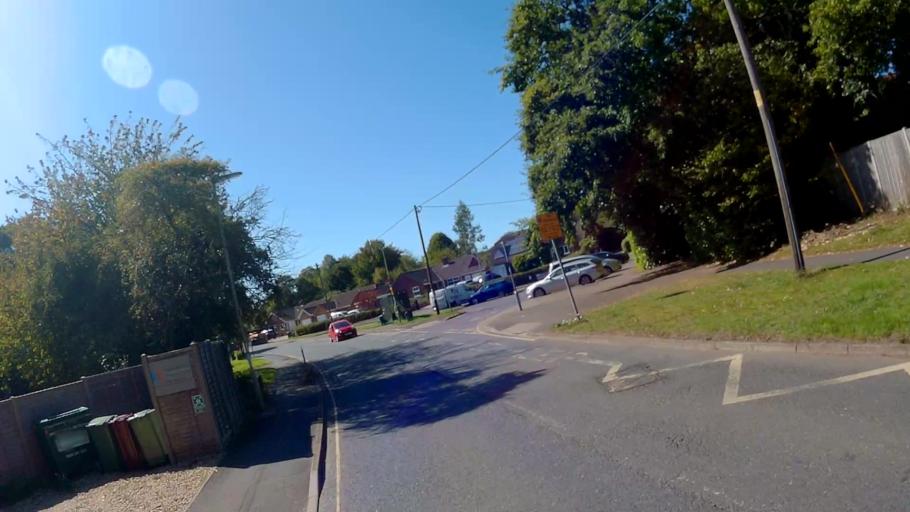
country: GB
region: England
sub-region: Hampshire
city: Overton
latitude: 51.2495
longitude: -1.1780
